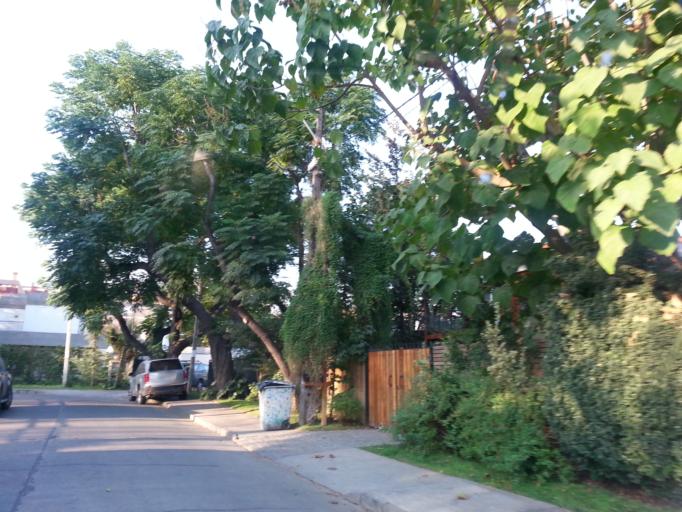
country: CL
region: Santiago Metropolitan
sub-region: Provincia de Santiago
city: Villa Presidente Frei, Nunoa, Santiago, Chile
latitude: -33.3891
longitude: -70.5915
